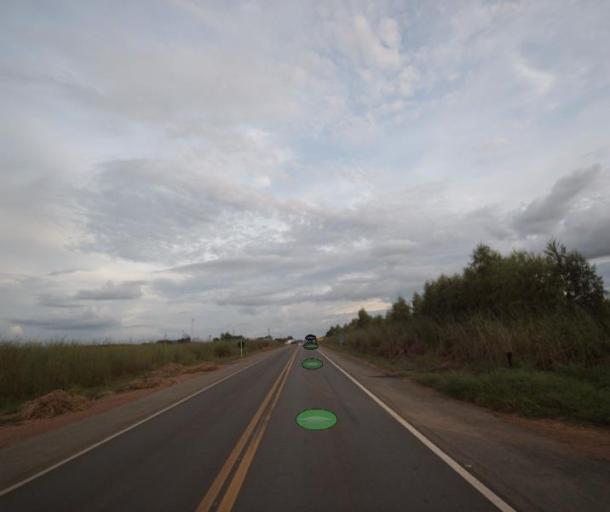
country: BR
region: Goias
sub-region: Barro Alto
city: Barro Alto
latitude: -15.2034
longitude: -48.7012
